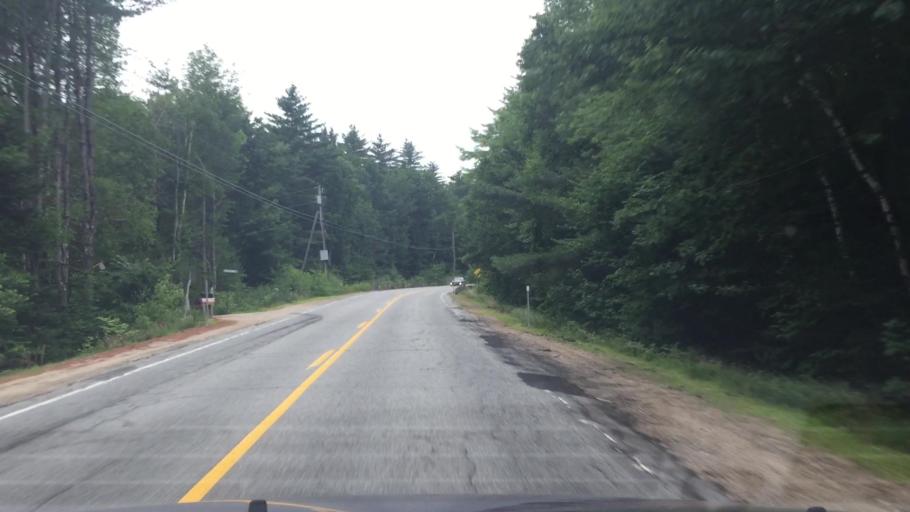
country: US
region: New Hampshire
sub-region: Carroll County
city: North Conway
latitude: 44.0903
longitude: -71.1645
